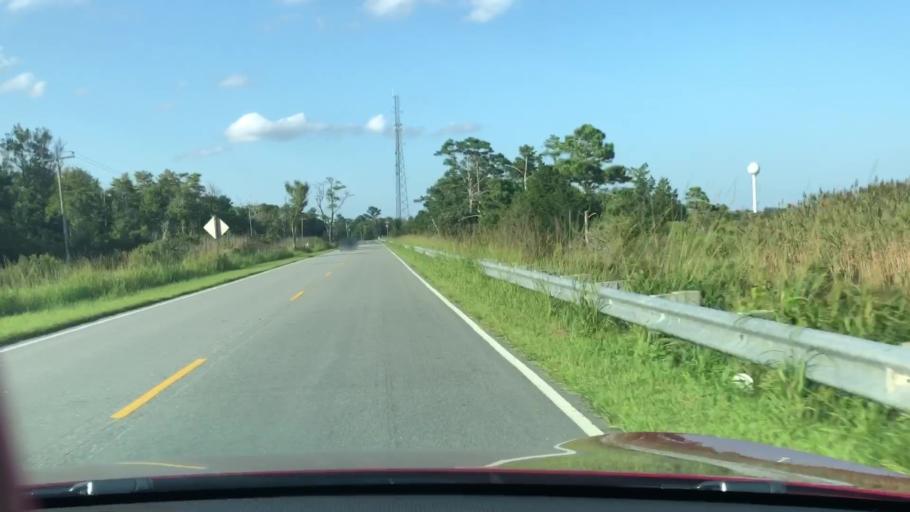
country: US
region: North Carolina
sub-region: Dare County
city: Wanchese
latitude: 35.7032
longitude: -75.7702
